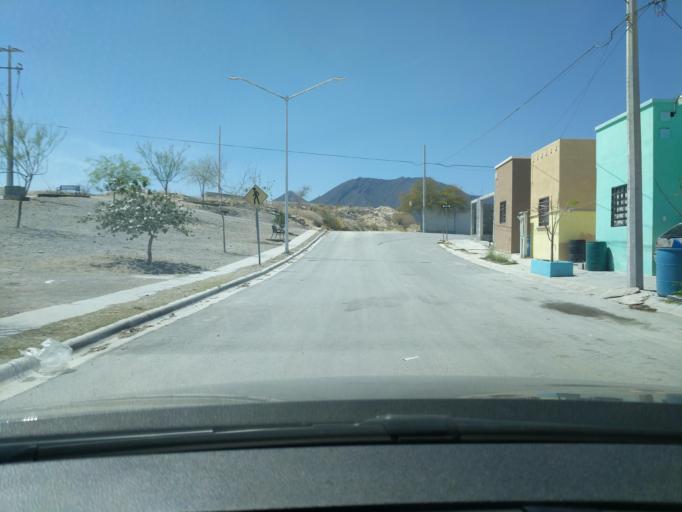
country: MX
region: Nuevo Leon
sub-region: Salinas Victoria
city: Las Torres
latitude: 25.9656
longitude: -100.3108
